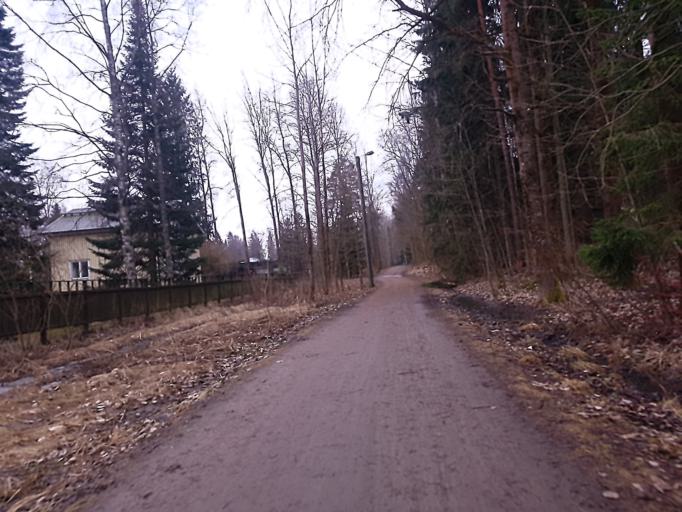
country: FI
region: Uusimaa
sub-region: Helsinki
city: Helsinki
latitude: 60.2371
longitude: 24.9146
